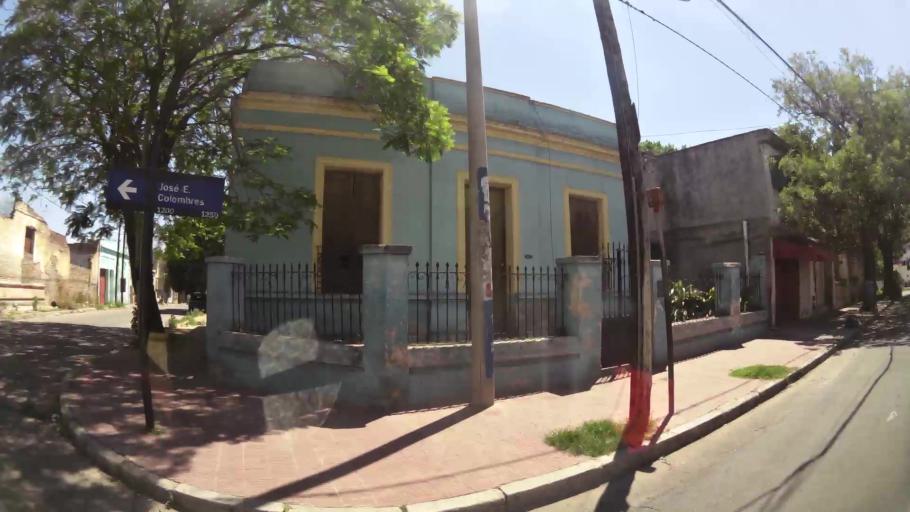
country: AR
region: Cordoba
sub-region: Departamento de Capital
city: Cordoba
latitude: -31.3924
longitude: -64.1968
